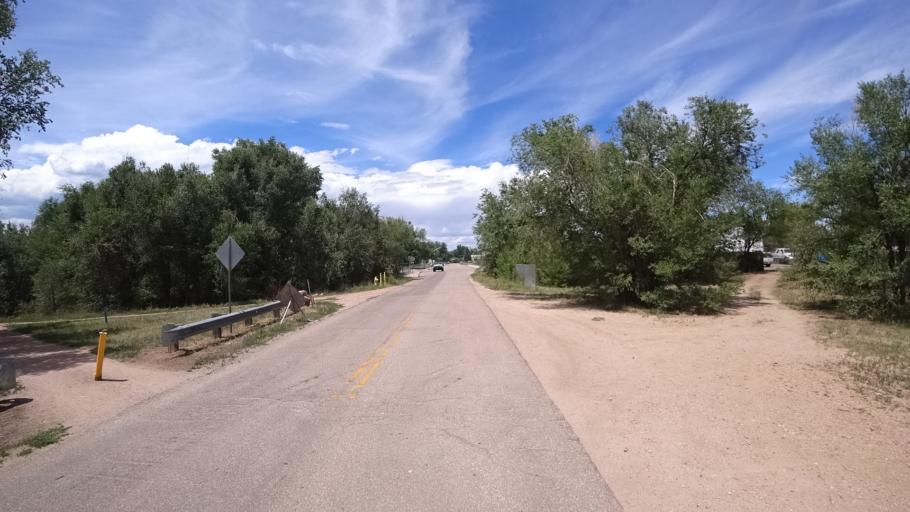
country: US
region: Colorado
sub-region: El Paso County
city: Security-Widefield
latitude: 38.7267
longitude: -104.7264
